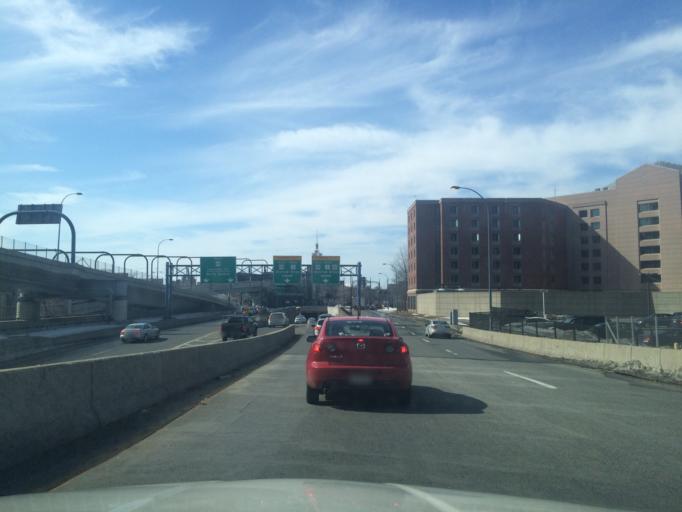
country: US
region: Massachusetts
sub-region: Suffolk County
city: Boston
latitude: 42.3663
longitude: -71.0650
